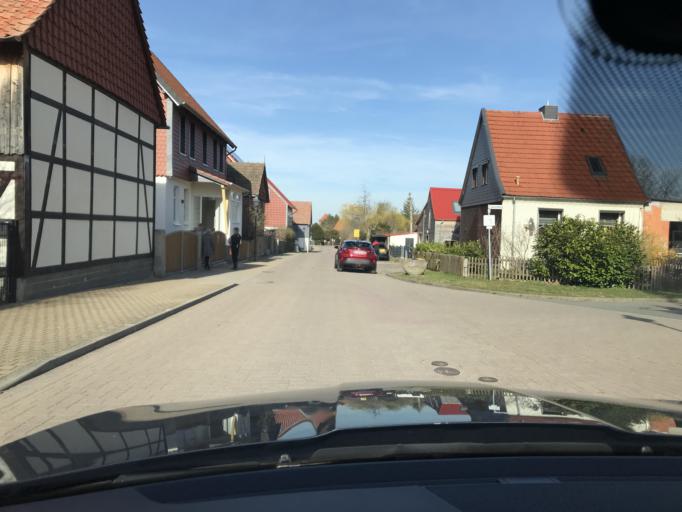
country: DE
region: Saxony-Anhalt
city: Darlingerode
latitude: 51.8434
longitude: 10.7250
